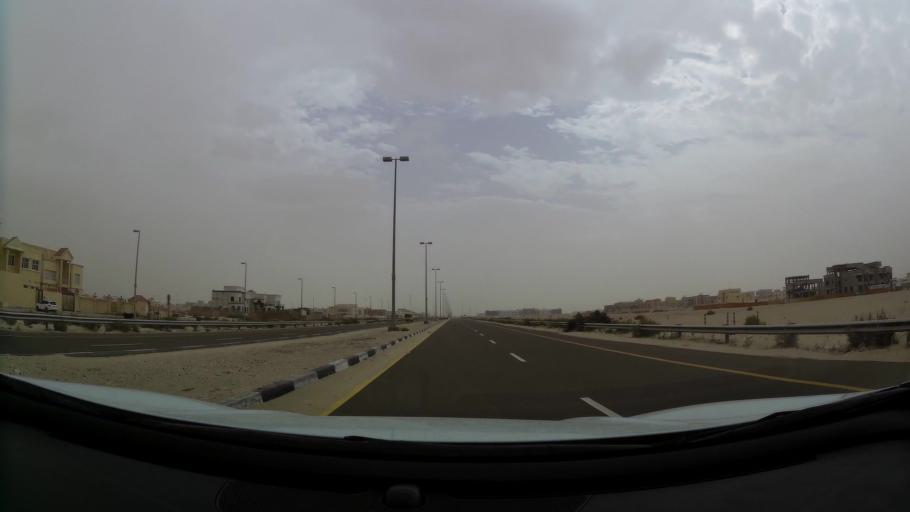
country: AE
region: Abu Dhabi
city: Abu Dhabi
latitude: 24.3628
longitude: 54.6974
